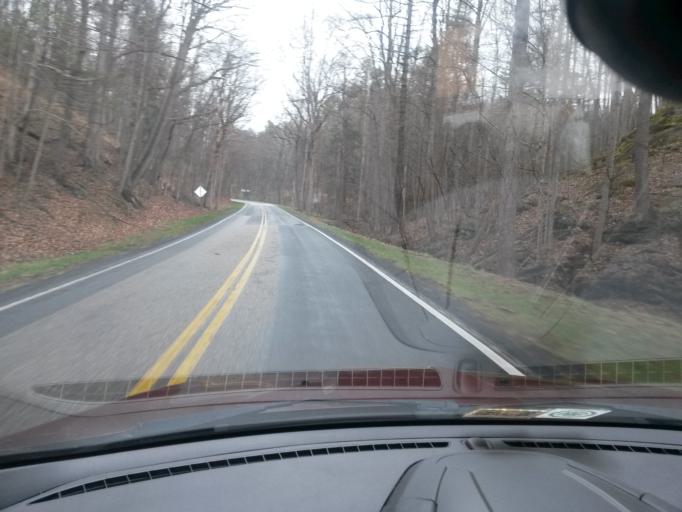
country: US
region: Virginia
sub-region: Bath County
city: Warm Springs
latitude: 37.9254
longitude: -79.7152
